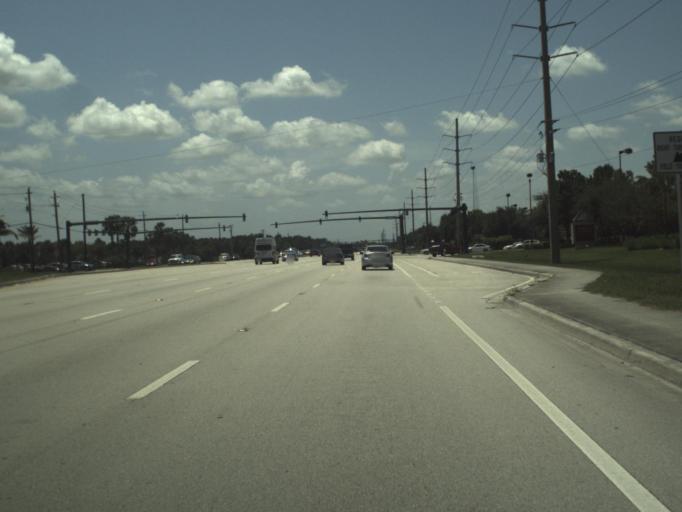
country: US
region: Florida
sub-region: Martin County
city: North River Shores
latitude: 27.2568
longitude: -80.2799
